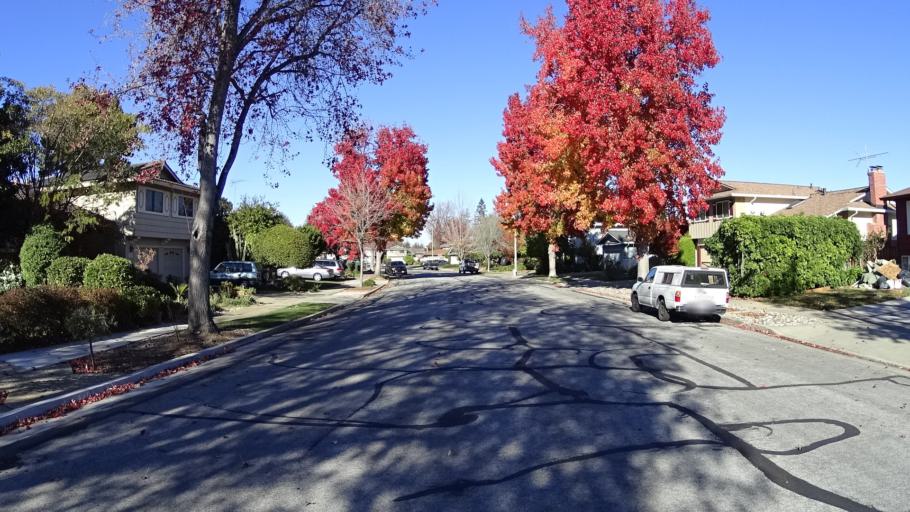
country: US
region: California
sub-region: Santa Clara County
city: Sunnyvale
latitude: 37.3500
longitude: -122.0251
